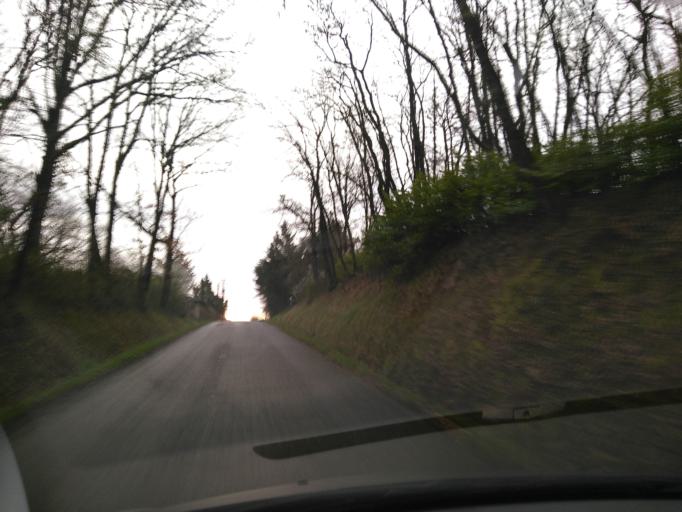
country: FR
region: Midi-Pyrenees
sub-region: Departement du Tarn-et-Garonne
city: Finhan
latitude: 43.8758
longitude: 1.1473
